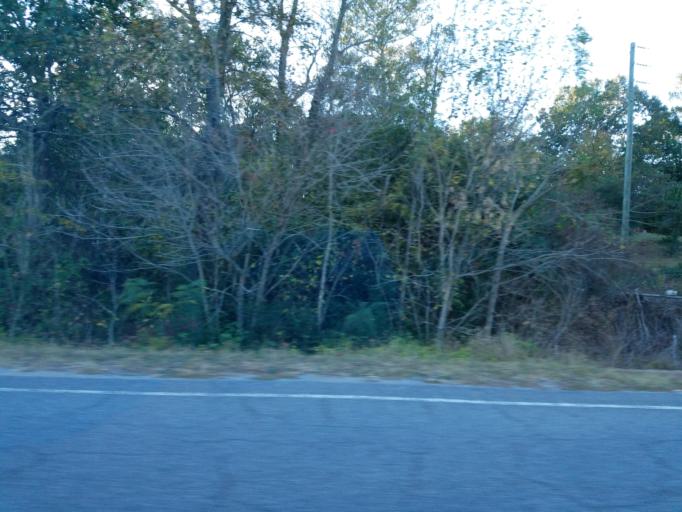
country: US
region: Georgia
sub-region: Bartow County
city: Adairsville
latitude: 34.3446
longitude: -84.9384
